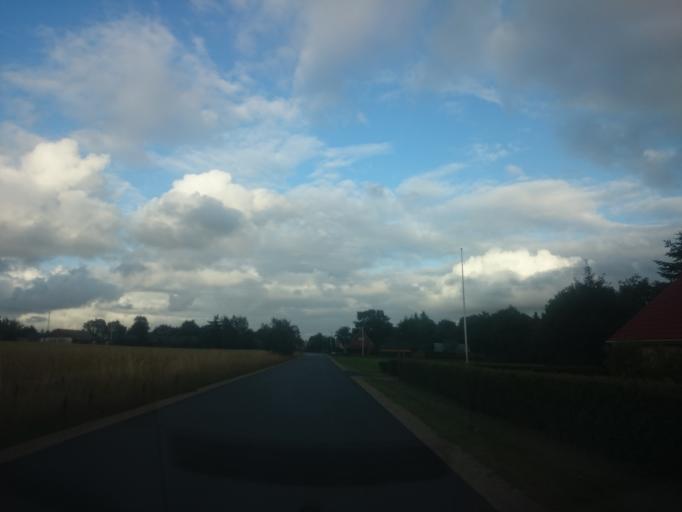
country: DK
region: South Denmark
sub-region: Billund Kommune
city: Billund
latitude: 55.6298
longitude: 9.0690
